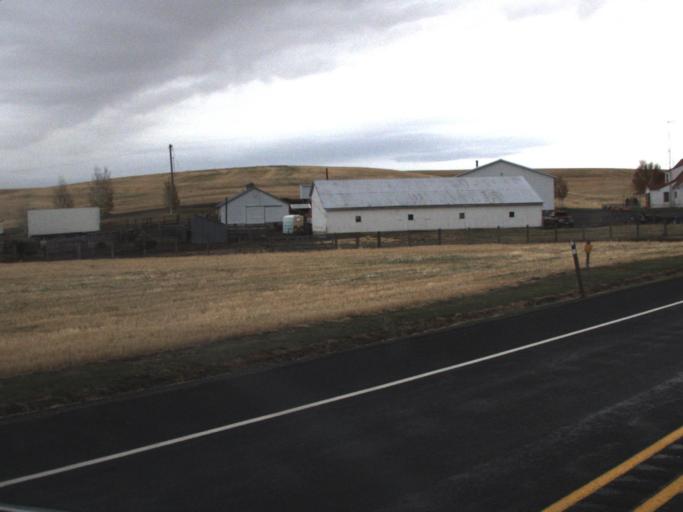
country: US
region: Washington
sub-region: Whitman County
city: Pullman
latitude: 46.5725
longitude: -117.1459
